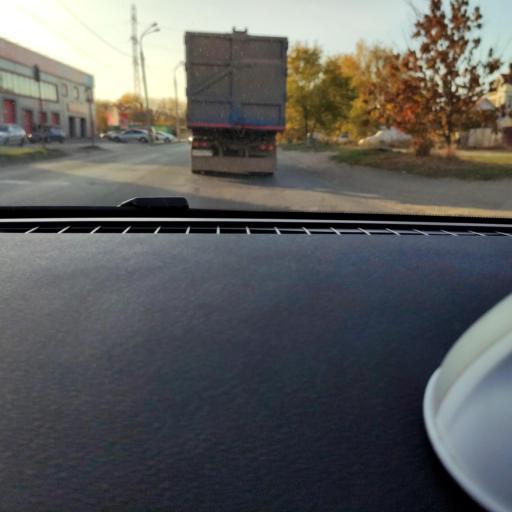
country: RU
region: Samara
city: Samara
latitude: 53.1342
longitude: 50.1183
